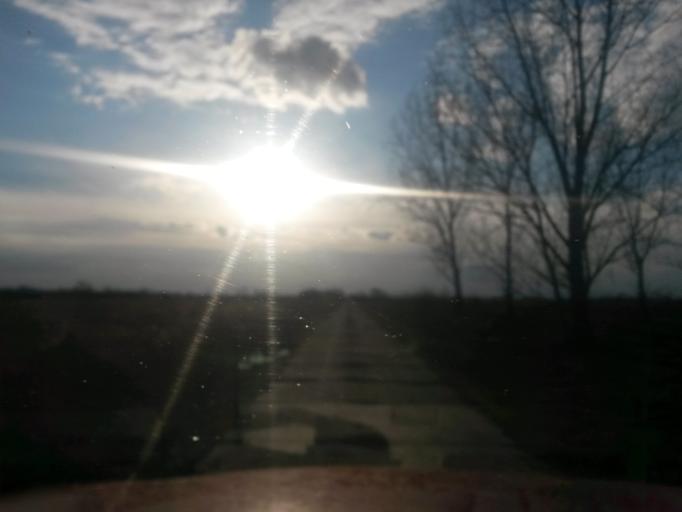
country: SK
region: Kosicky
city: Sobrance
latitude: 48.7054
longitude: 22.0989
